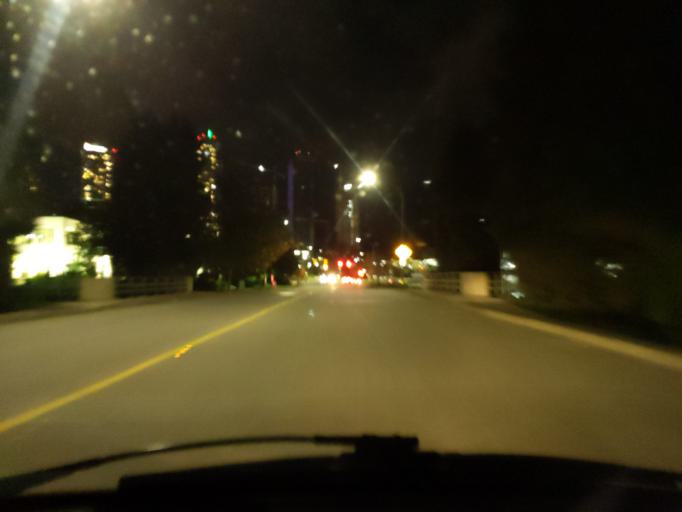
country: CA
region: British Columbia
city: Burnaby
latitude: 49.2595
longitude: -123.0075
